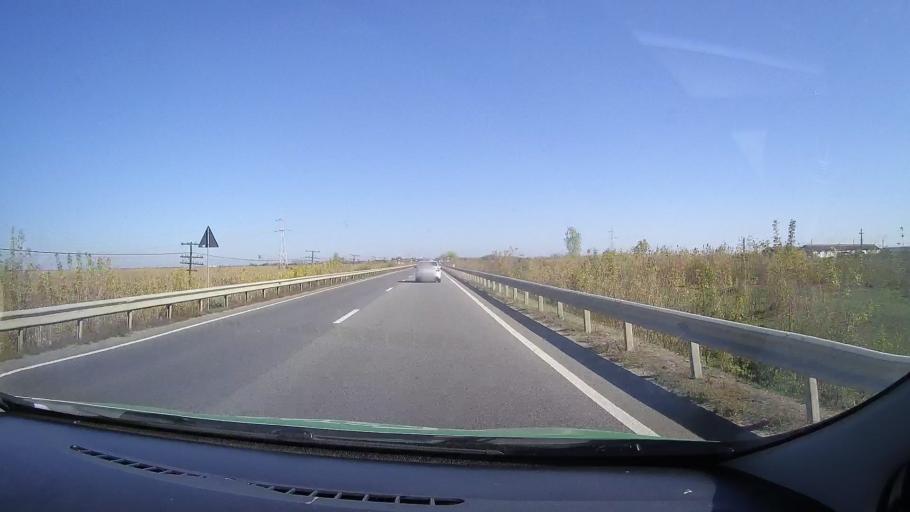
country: RO
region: Satu Mare
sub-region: Comuna Doba
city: Doba
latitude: 47.7340
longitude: 22.6935
